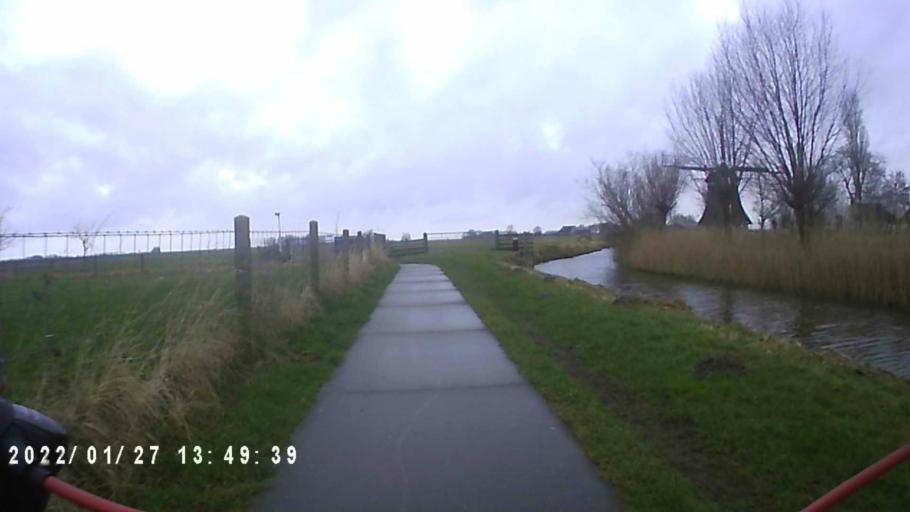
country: NL
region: Friesland
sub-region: Gemeente Kollumerland en Nieuwkruisland
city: Kollum
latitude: 53.3056
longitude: 6.1950
